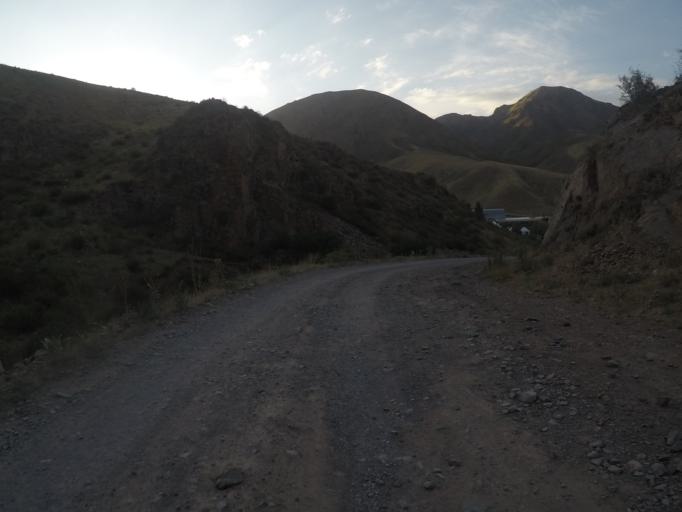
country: KG
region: Chuy
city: Bishkek
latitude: 42.6695
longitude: 74.6455
